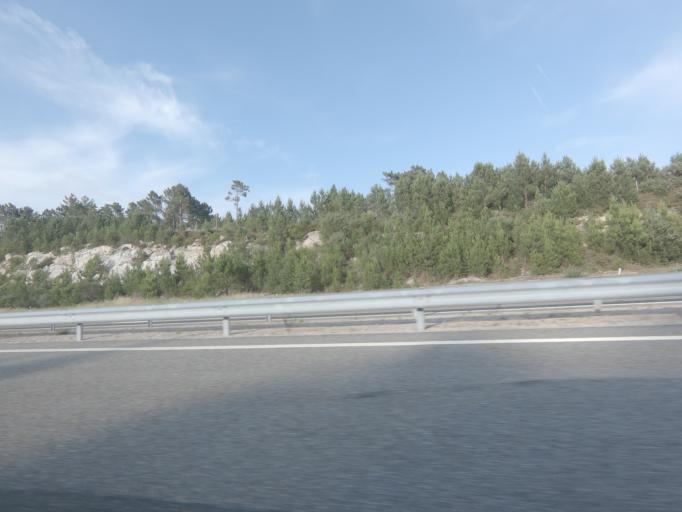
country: PT
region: Vila Real
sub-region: Vila Pouca de Aguiar
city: Vila Pouca de Aguiar
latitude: 41.5017
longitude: -7.6561
